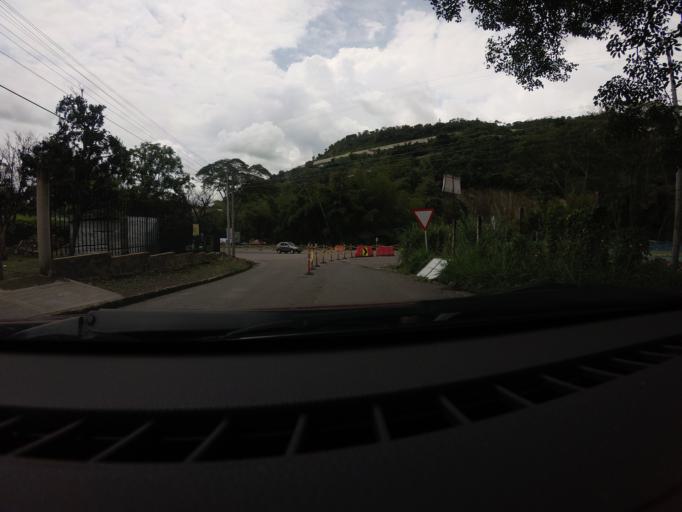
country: CO
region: Cundinamarca
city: La Vega
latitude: 4.9856
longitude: -74.3261
